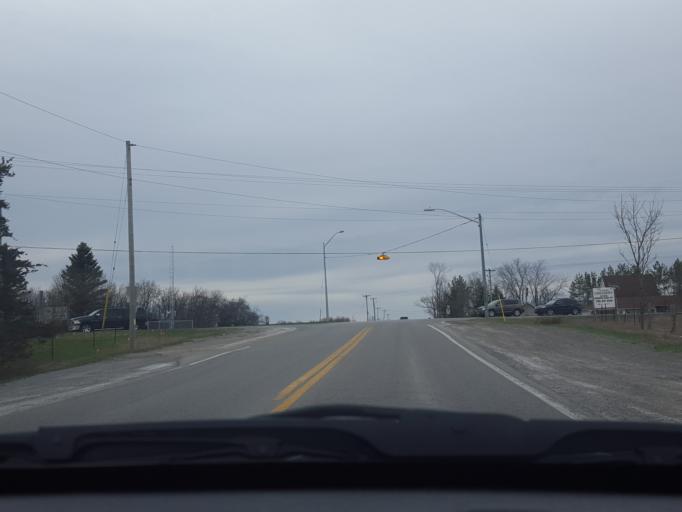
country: CA
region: Ontario
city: Uxbridge
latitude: 44.3181
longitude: -79.1803
